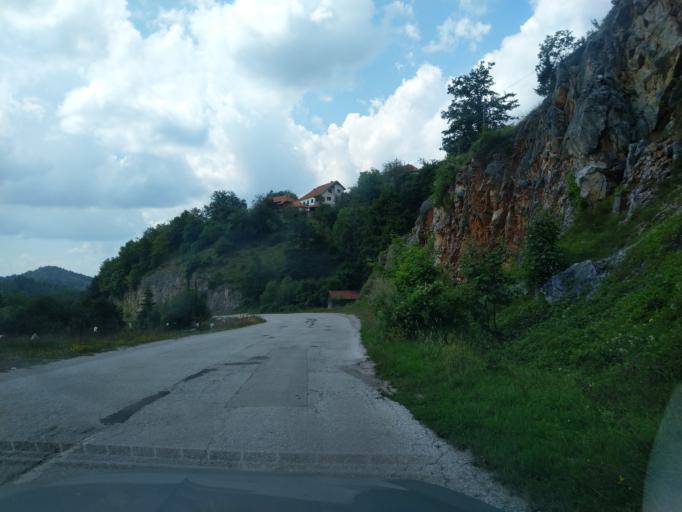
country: RS
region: Central Serbia
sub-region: Zlatiborski Okrug
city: Nova Varos
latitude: 43.5395
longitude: 19.9083
